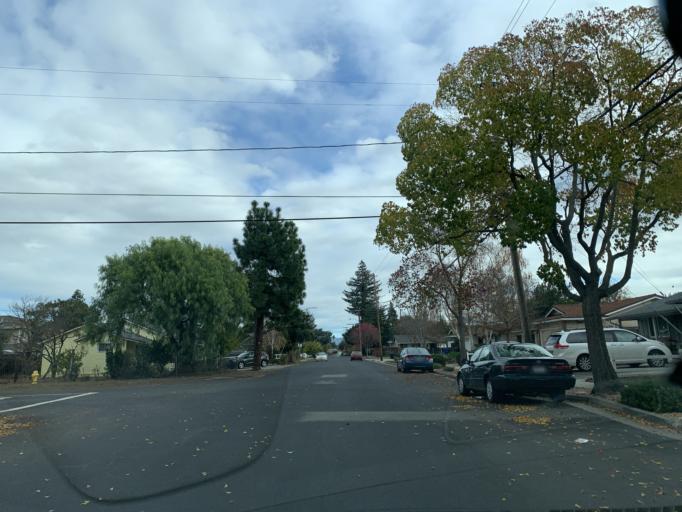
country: US
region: California
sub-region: Santa Clara County
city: Campbell
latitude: 37.2756
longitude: -121.9690
